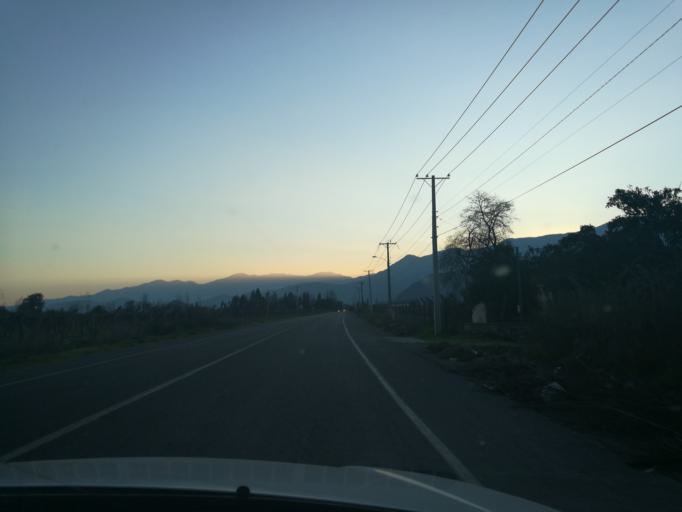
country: CL
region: O'Higgins
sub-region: Provincia de Cachapoal
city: Graneros
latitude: -34.0380
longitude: -70.6882
